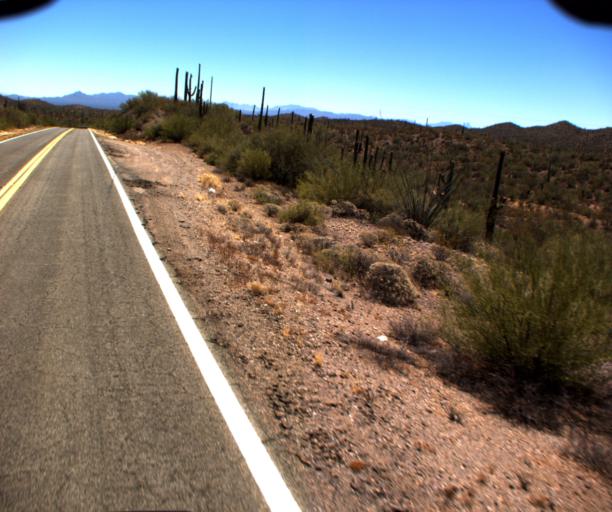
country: US
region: Arizona
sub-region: Pima County
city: Sells
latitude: 32.1741
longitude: -112.1703
